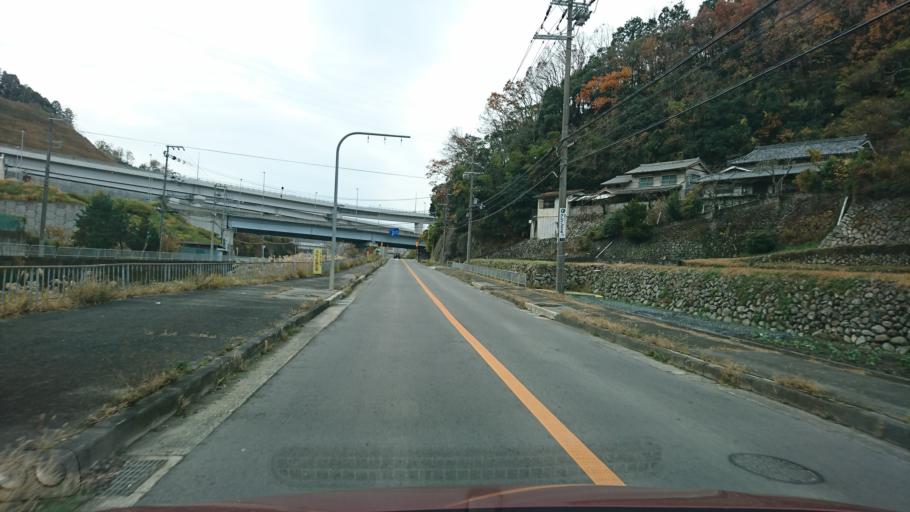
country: JP
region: Osaka
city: Mino
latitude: 34.8785
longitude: 135.4581
